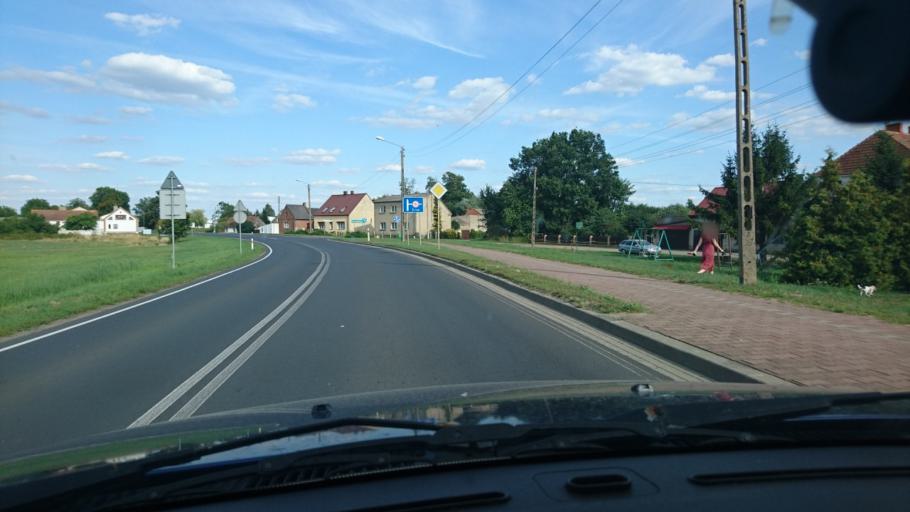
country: PL
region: Greater Poland Voivodeship
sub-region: Powiat krotoszynski
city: Kobylin
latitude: 51.7157
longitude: 17.2347
